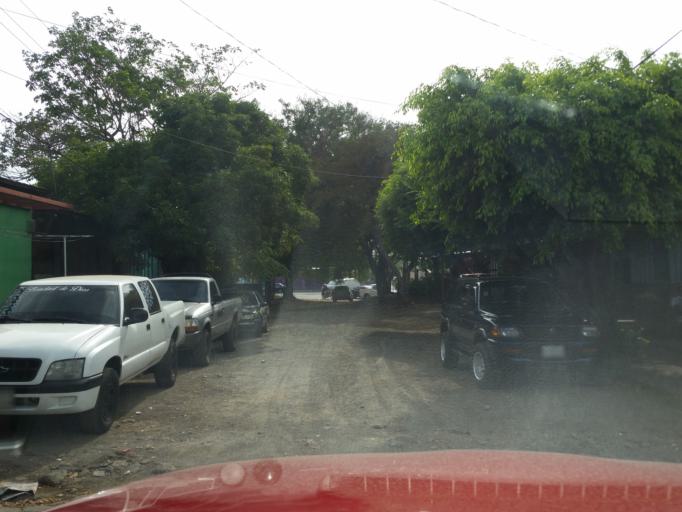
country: NI
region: Managua
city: Managua
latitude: 12.1356
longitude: -86.2529
